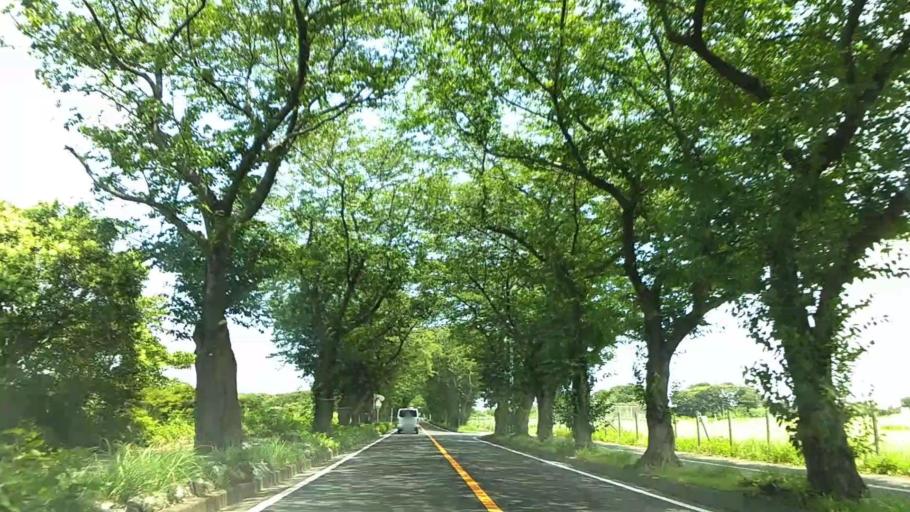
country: JP
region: Kanagawa
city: Minami-rinkan
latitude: 35.4871
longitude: 139.4804
